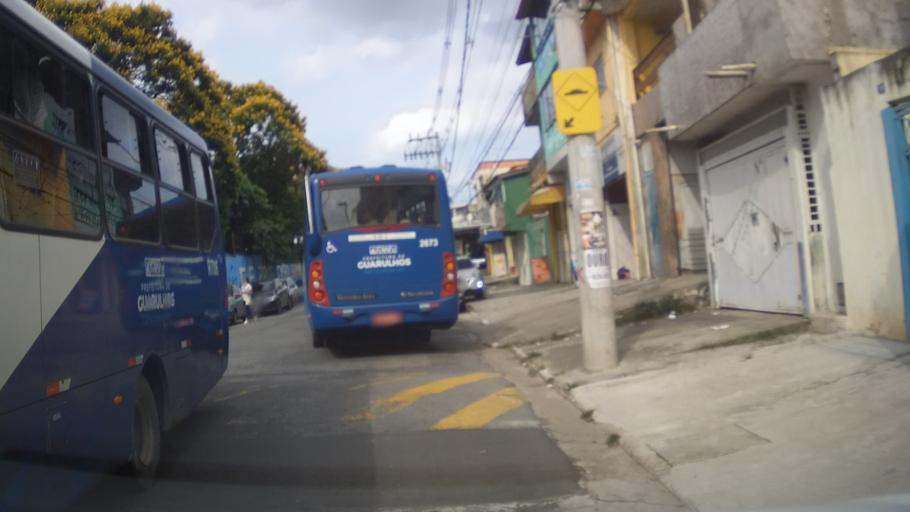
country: BR
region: Sao Paulo
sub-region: Guarulhos
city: Guarulhos
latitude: -23.4054
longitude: -46.4539
